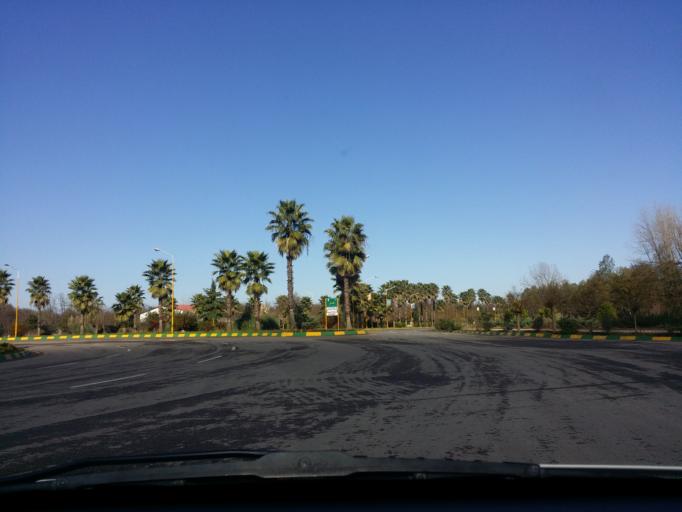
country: IR
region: Mazandaran
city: Chalus
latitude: 36.6831
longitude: 51.3055
